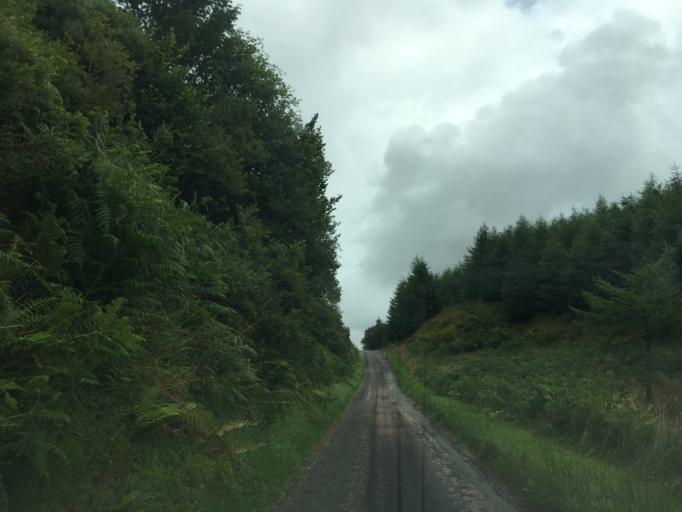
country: GB
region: Scotland
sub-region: Argyll and Bute
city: Oban
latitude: 56.2533
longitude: -5.4112
